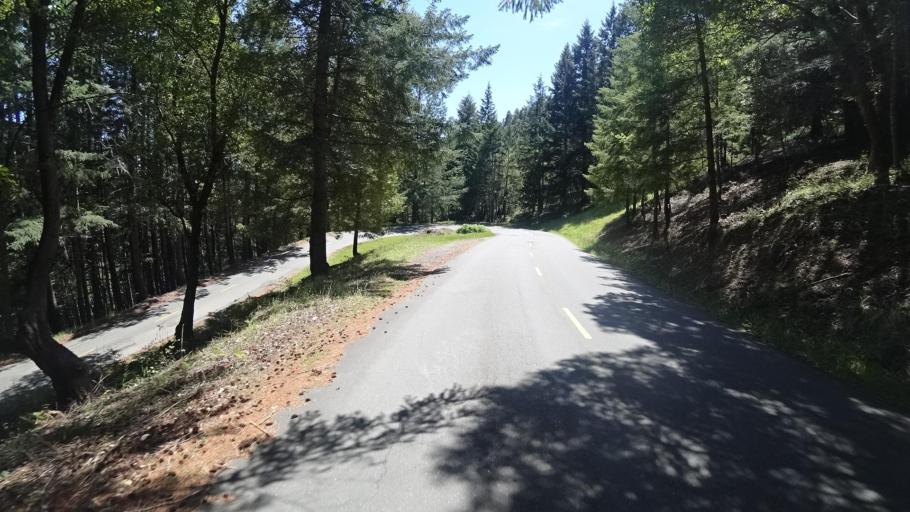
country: US
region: California
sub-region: Humboldt County
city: Rio Dell
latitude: 40.3261
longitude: -124.0468
